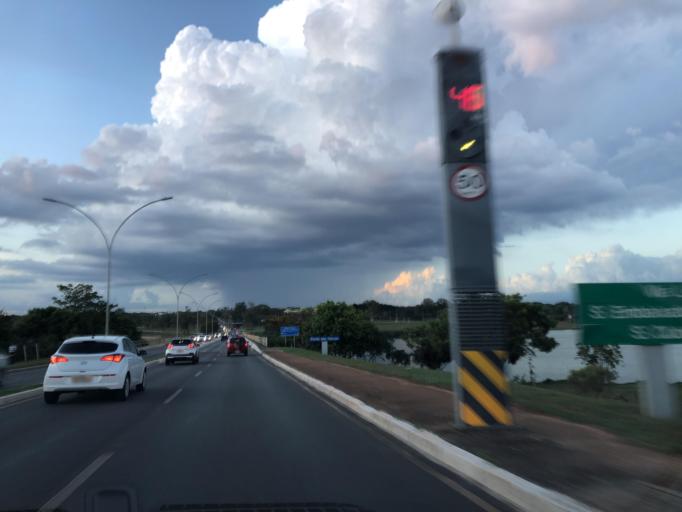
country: BR
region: Federal District
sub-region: Brasilia
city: Brasilia
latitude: -15.8417
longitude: -47.8970
